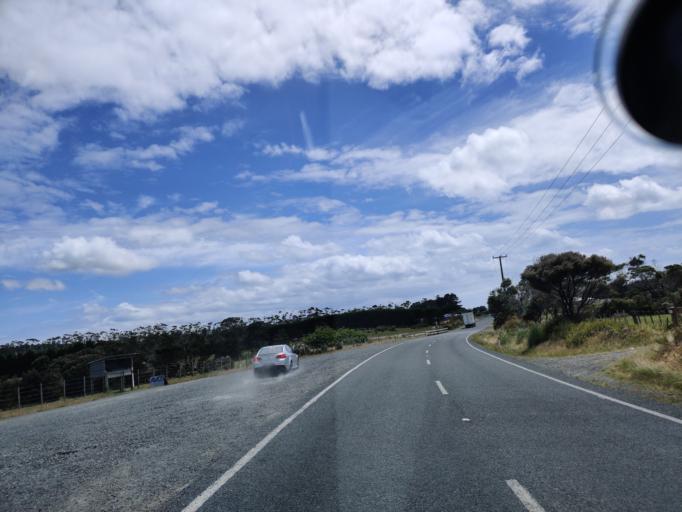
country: NZ
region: Northland
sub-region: Far North District
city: Kaitaia
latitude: -34.8286
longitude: 173.1279
